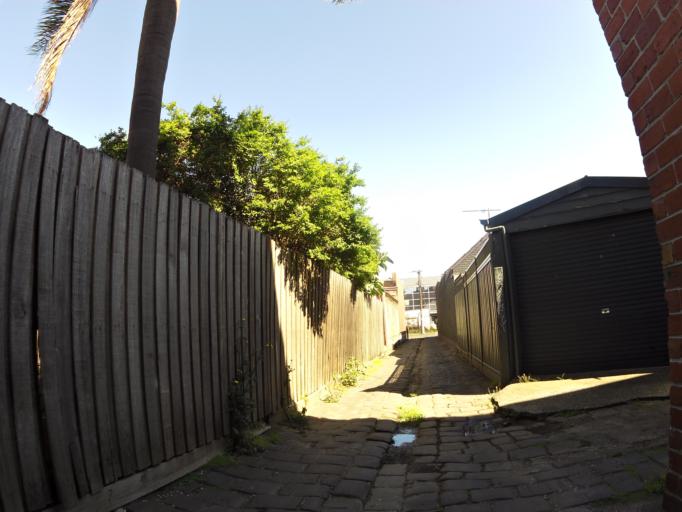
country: AU
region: Victoria
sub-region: Yarra
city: Richmond
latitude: -37.8093
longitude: 145.0029
